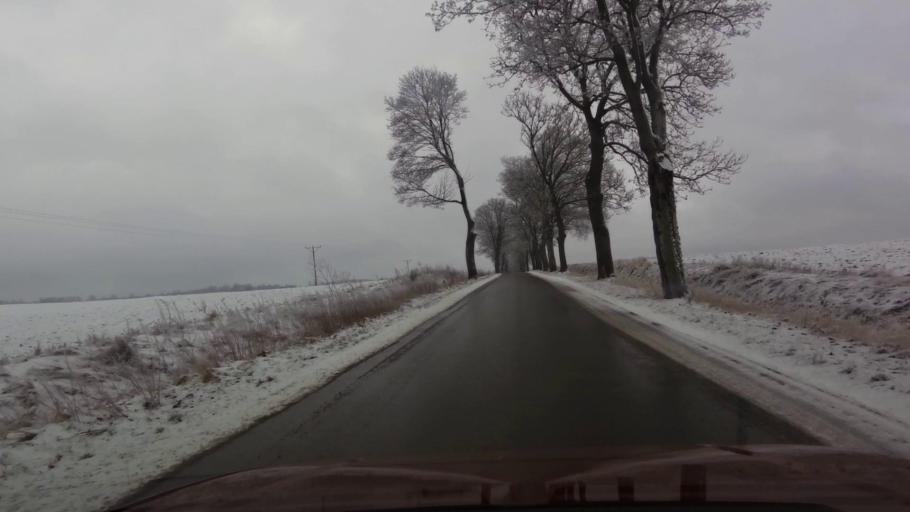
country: PL
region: West Pomeranian Voivodeship
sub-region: Powiat swidwinski
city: Rabino
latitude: 53.8452
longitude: 15.9569
